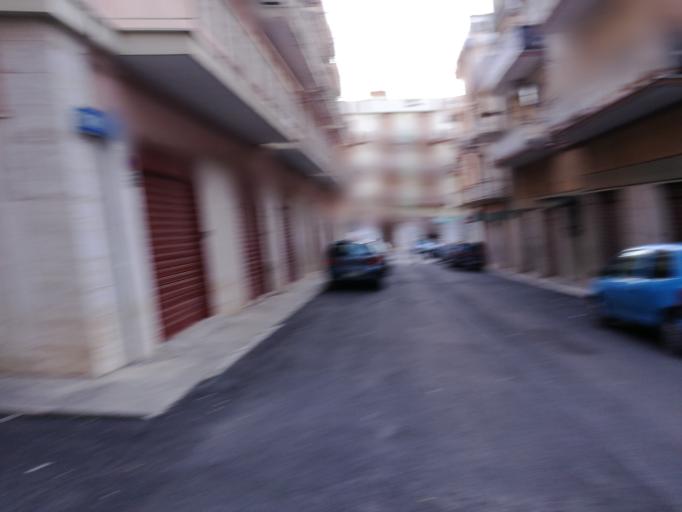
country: IT
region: Apulia
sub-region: Provincia di Bari
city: Corato
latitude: 41.1480
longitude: 16.4156
